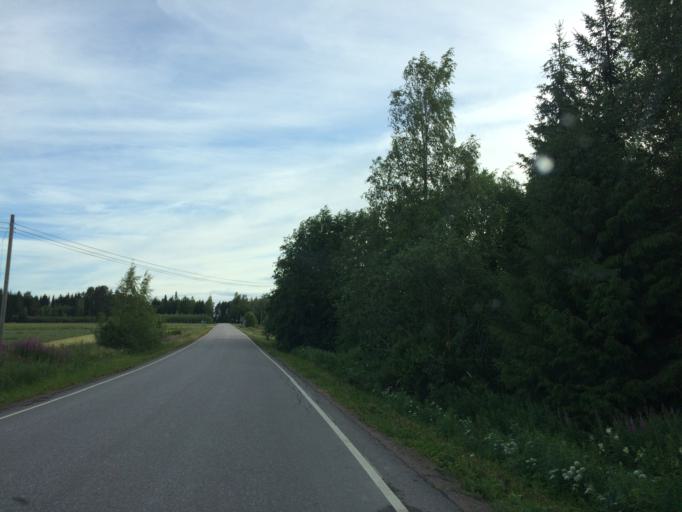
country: FI
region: Haeme
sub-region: Haemeenlinna
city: Janakkala
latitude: 60.8729
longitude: 24.5630
